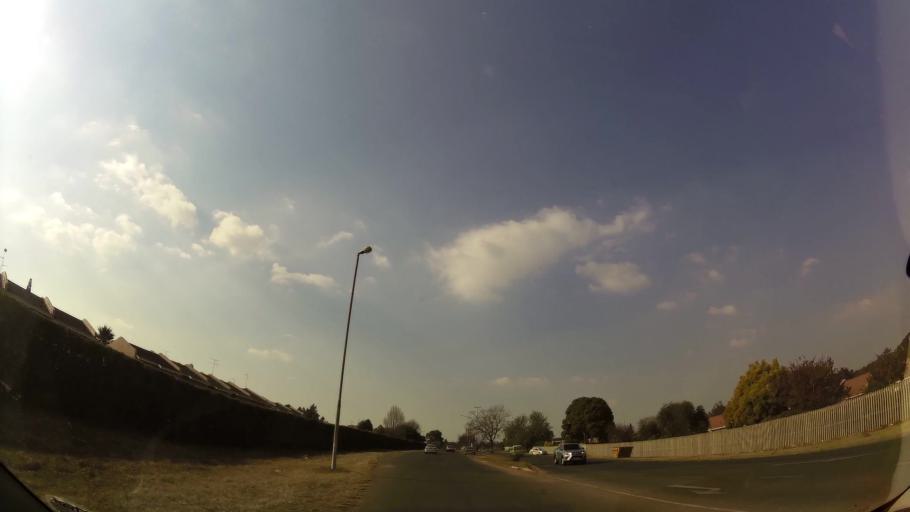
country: ZA
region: Gauteng
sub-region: Ekurhuleni Metropolitan Municipality
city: Benoni
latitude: -26.1381
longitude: 28.2896
